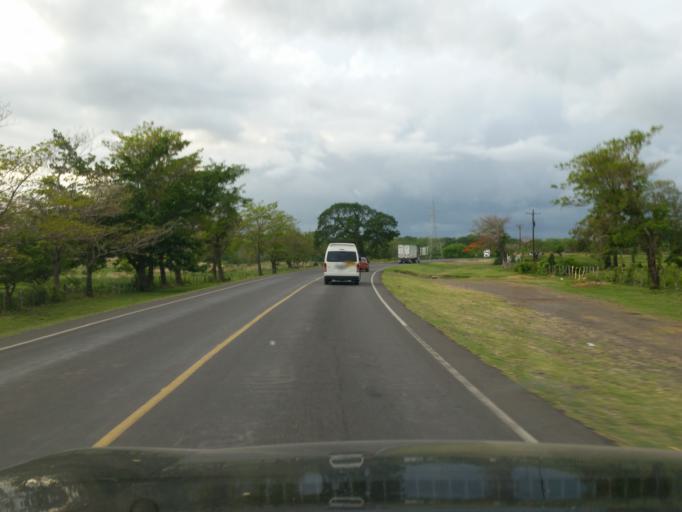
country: NI
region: Granada
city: Nandaime
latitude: 11.7163
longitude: -86.0121
